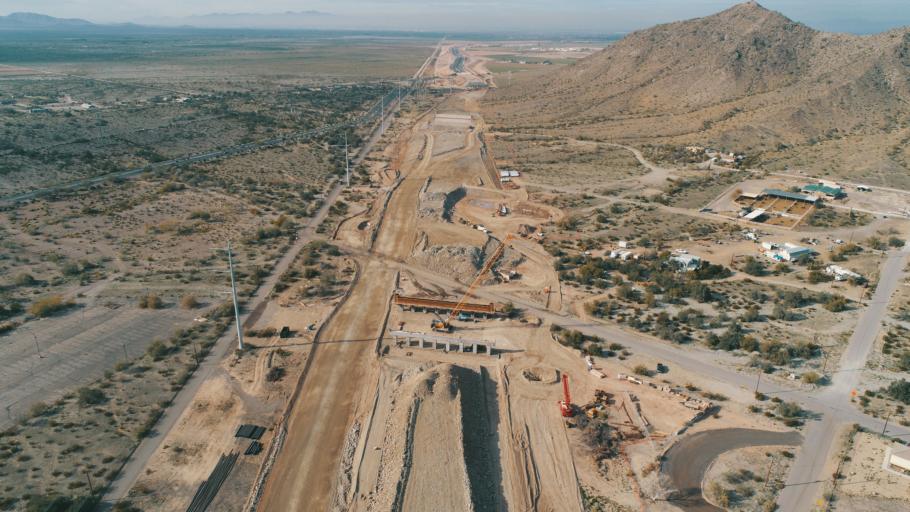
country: US
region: Arizona
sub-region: Maricopa County
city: Laveen
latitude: 33.3137
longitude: -112.1559
